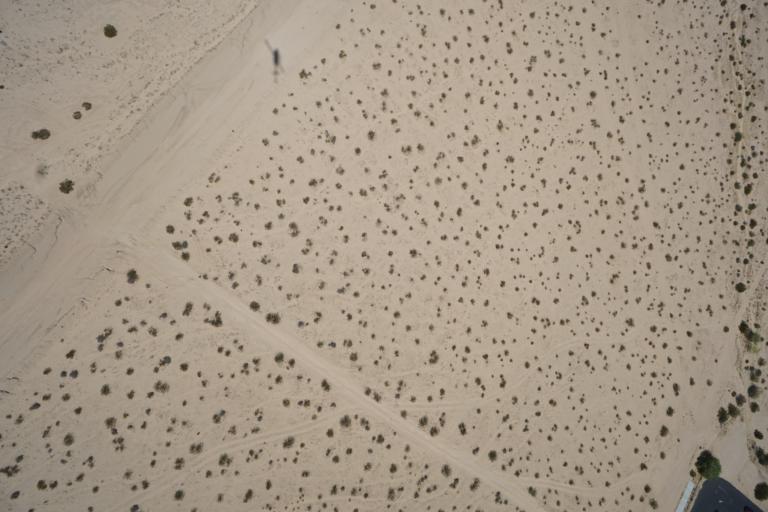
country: US
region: California
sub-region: San Bernardino County
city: Twentynine Palms
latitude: 34.1538
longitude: -116.0431
